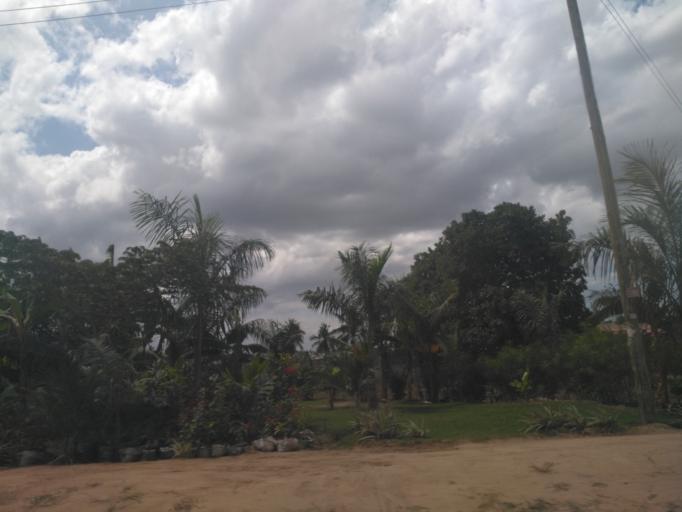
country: TZ
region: Dar es Salaam
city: Dar es Salaam
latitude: -6.9067
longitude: 39.2365
